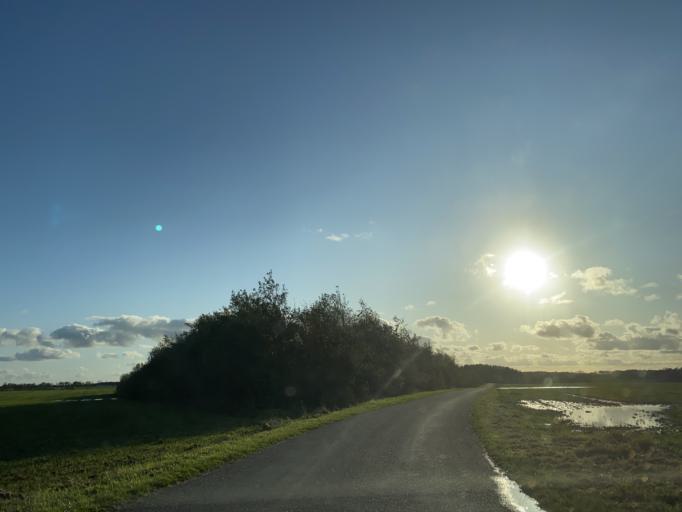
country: DK
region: Central Jutland
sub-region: Viborg Kommune
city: Bjerringbro
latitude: 56.3280
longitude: 9.7090
